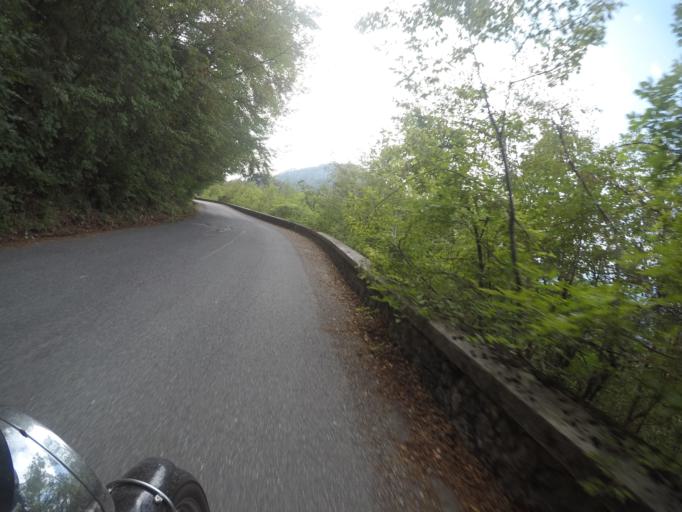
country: IT
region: Tuscany
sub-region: Provincia di Massa-Carrara
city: Fosdinovo
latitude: 44.1254
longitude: 10.0946
